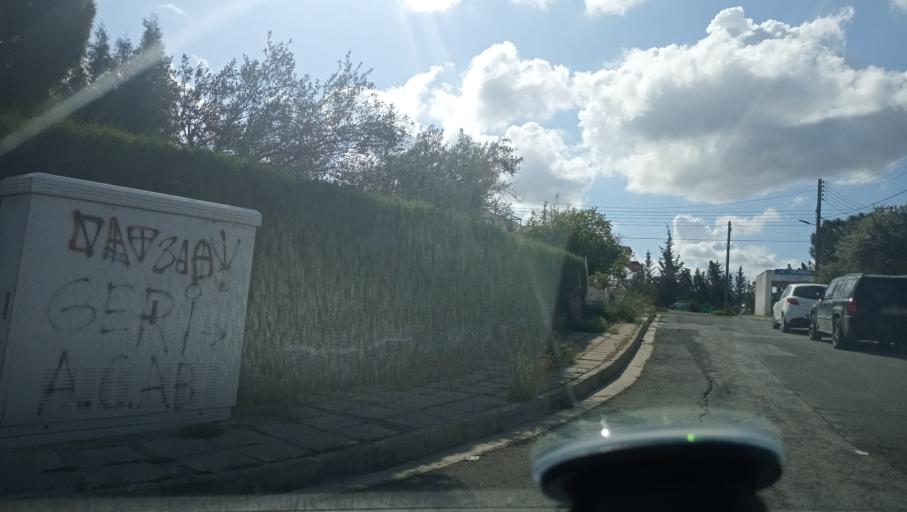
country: CY
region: Lefkosia
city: Geri
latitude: 35.1026
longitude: 33.4071
